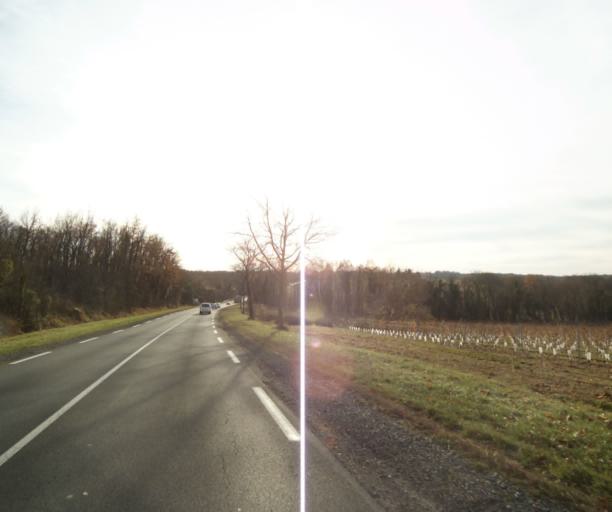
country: FR
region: Poitou-Charentes
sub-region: Departement de la Charente-Maritime
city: Saint-Hilaire-de-Villefranche
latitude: 45.8162
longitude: -0.5468
